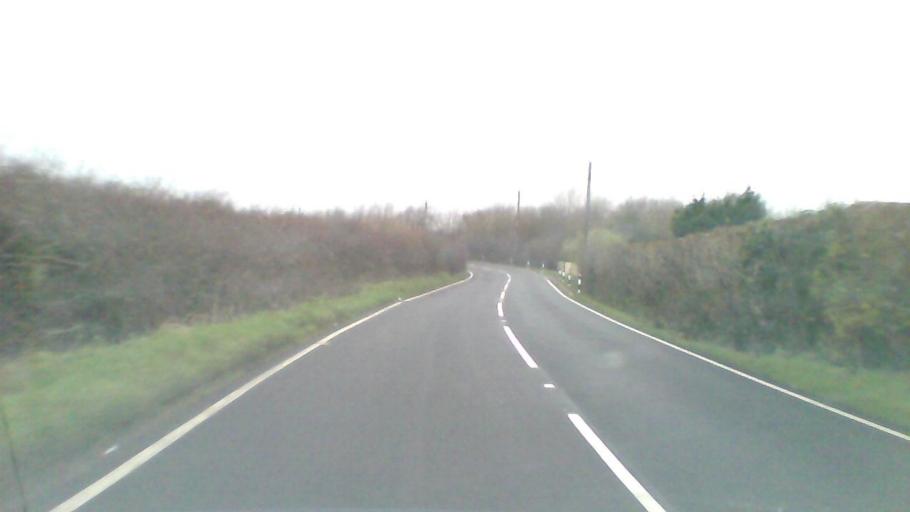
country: GB
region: England
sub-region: Isle of Wight
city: Newport
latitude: 50.6888
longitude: -1.2481
